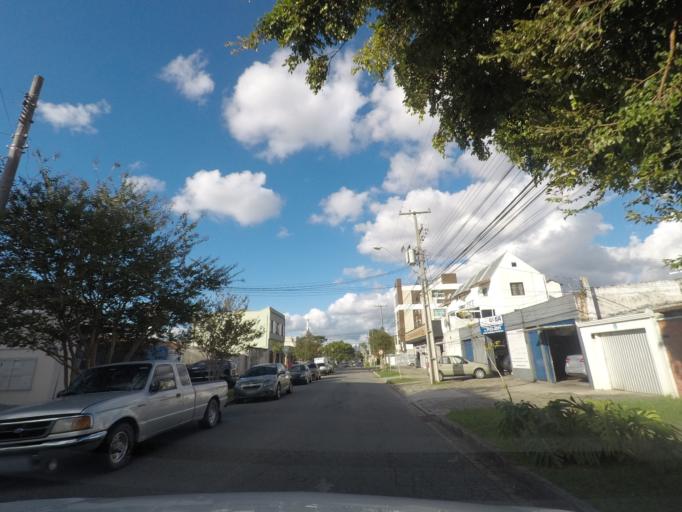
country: BR
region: Parana
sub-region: Curitiba
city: Curitiba
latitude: -25.4485
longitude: -49.2685
